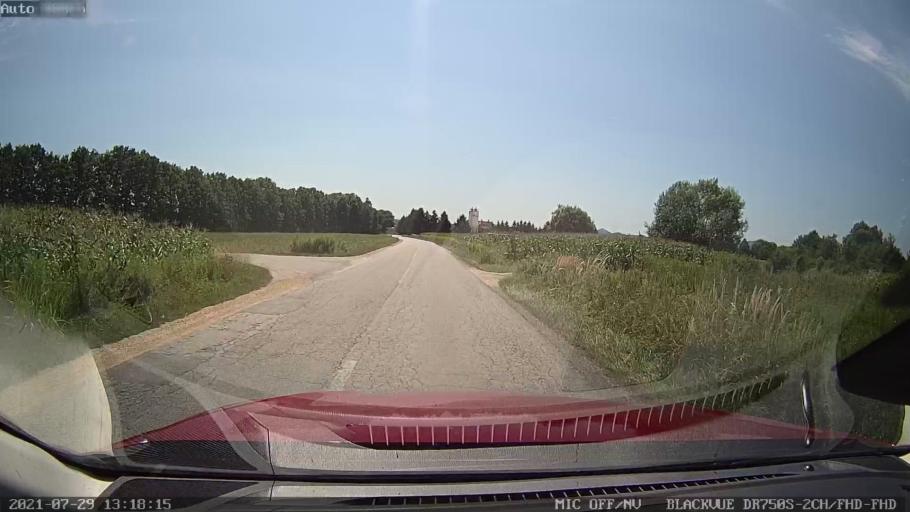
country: HR
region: Varazdinska
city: Varazdin
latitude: 46.2715
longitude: 16.3818
